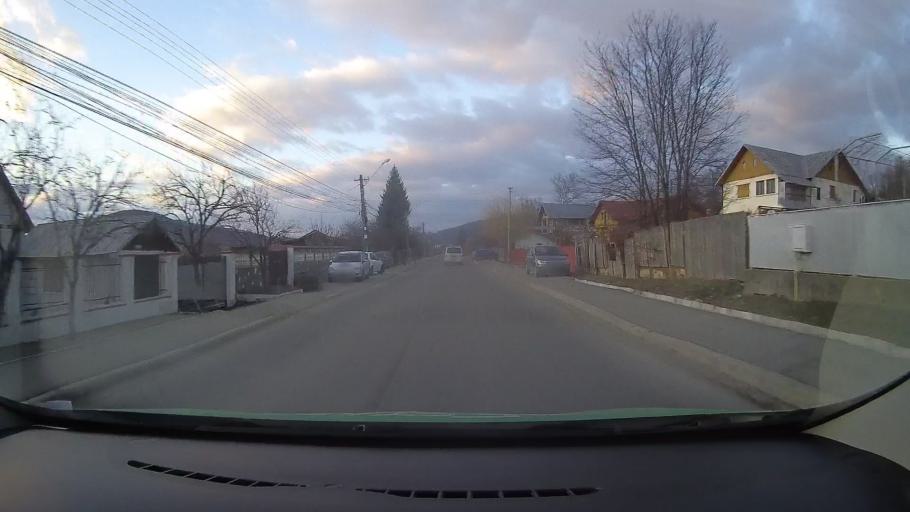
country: RO
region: Dambovita
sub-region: Municipiul Moreni
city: Moreni
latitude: 44.9983
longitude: 25.6478
